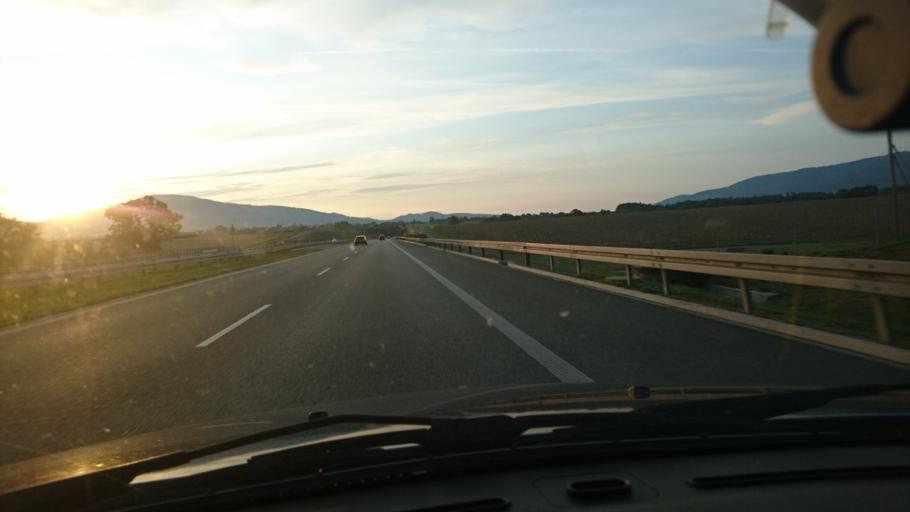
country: PL
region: Silesian Voivodeship
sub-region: Powiat zywiecki
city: Lodygowice
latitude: 49.7016
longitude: 19.1272
